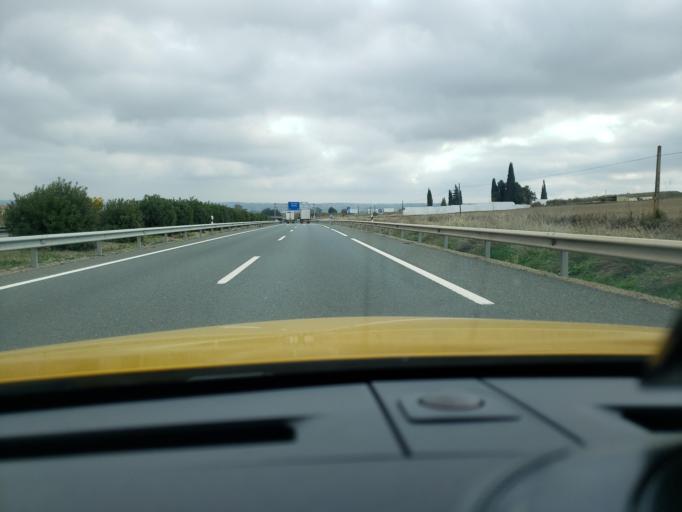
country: ES
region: Andalusia
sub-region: Provincia de Sevilla
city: Carrion de los Cespedes
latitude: 37.3608
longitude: -6.2793
